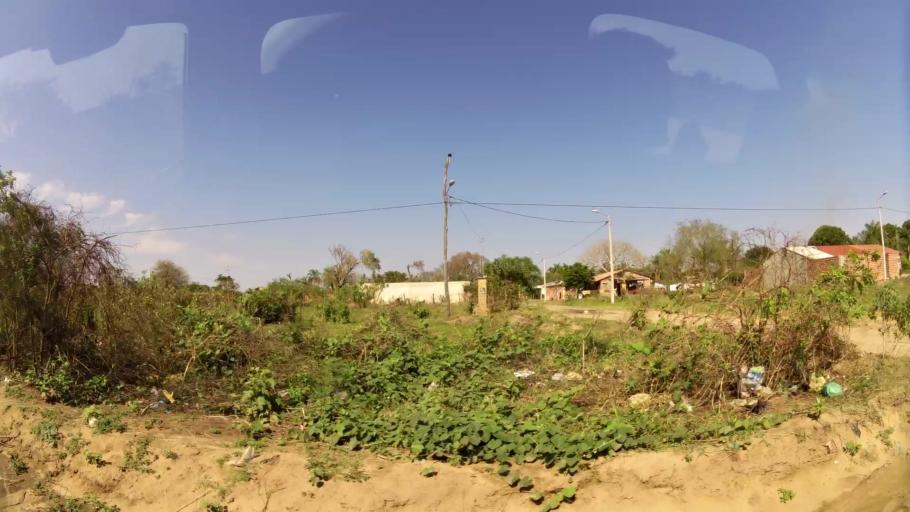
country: BO
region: Santa Cruz
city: Cotoca
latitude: -17.7131
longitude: -63.0637
